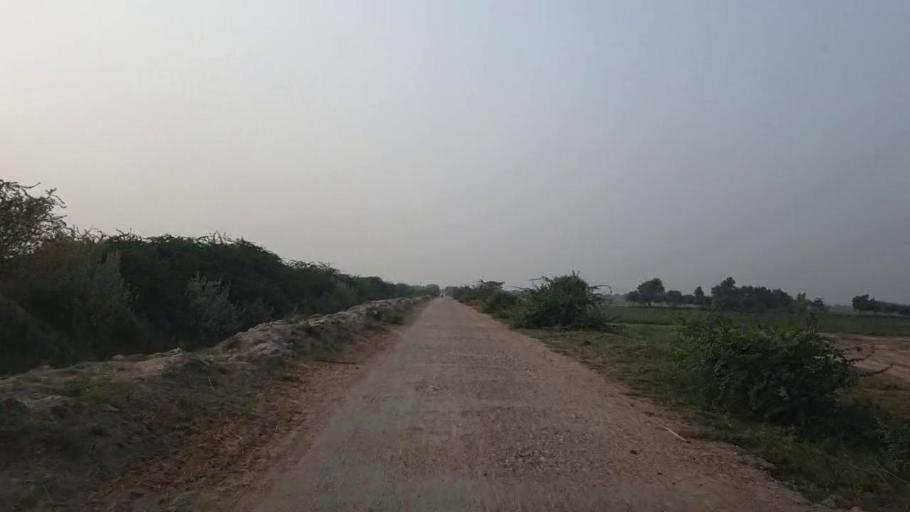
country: PK
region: Sindh
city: Mirpur Batoro
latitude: 24.6464
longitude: 68.3926
